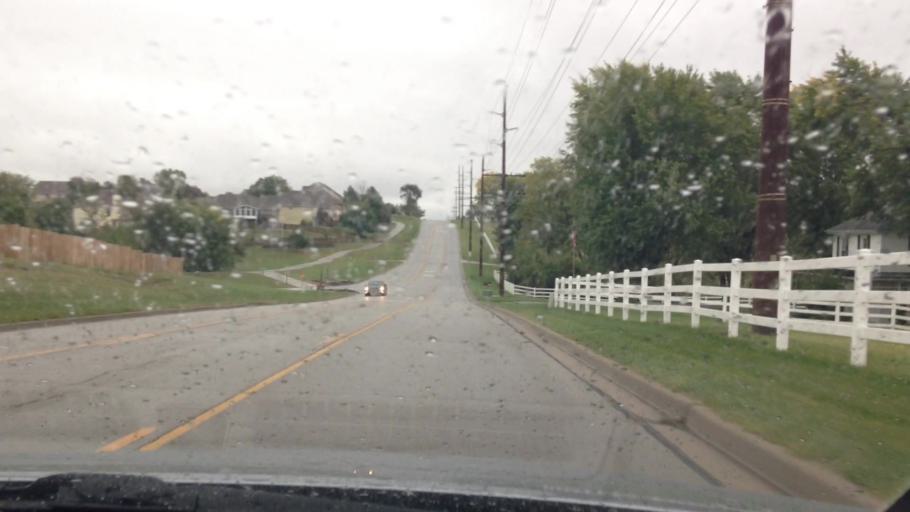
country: US
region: Missouri
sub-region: Platte County
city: Platte City
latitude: 39.3393
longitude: -94.7746
